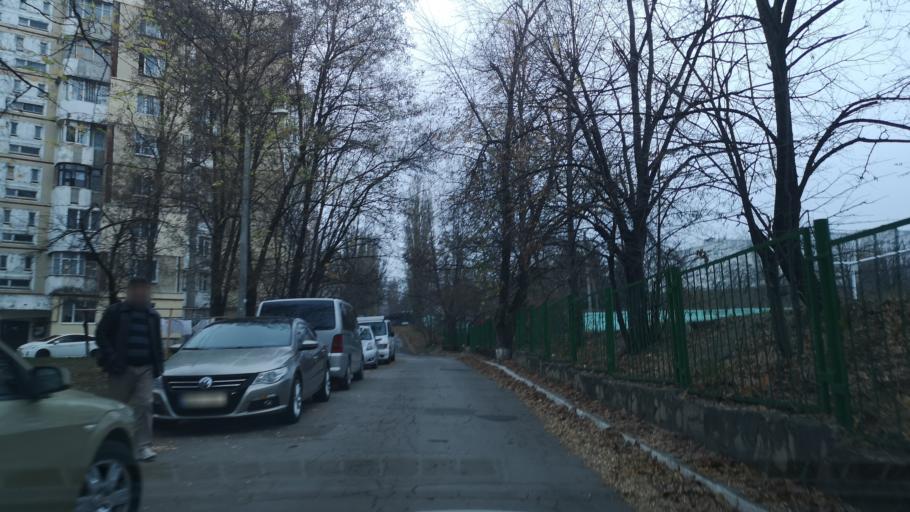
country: MD
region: Chisinau
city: Chisinau
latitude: 46.9756
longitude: 28.8649
